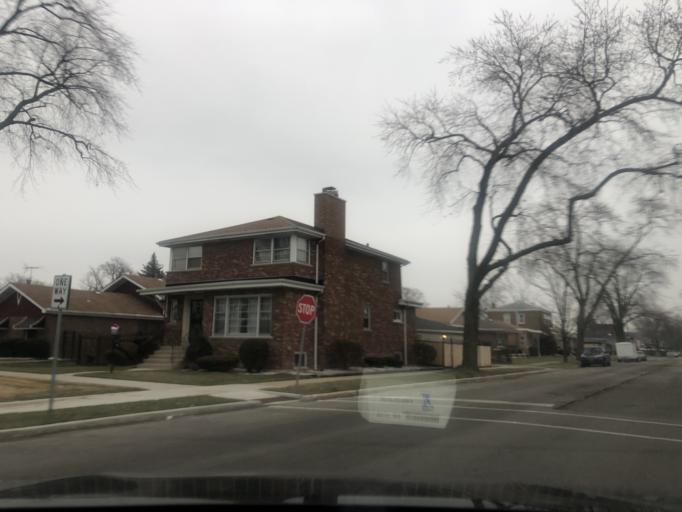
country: US
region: Illinois
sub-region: Cook County
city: Calumet Park
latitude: 41.7328
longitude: -87.6161
